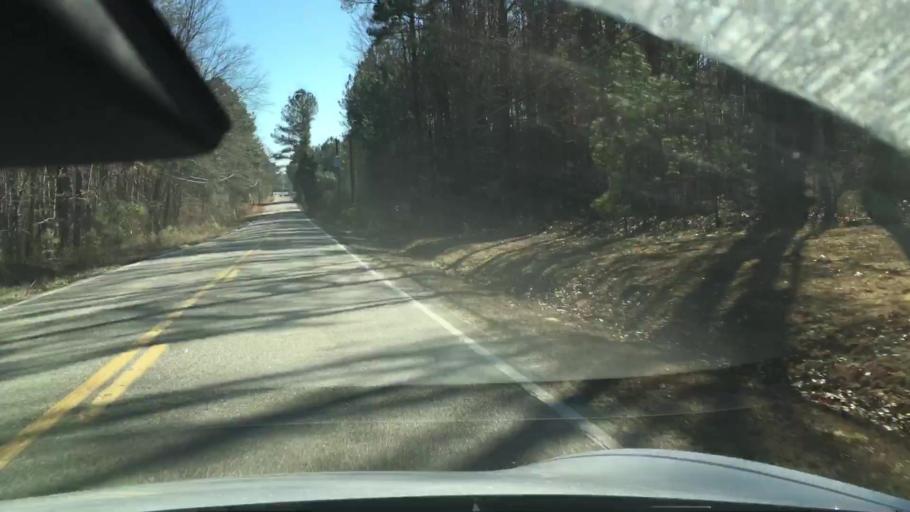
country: US
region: Virginia
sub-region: Henrico County
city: Short Pump
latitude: 37.5723
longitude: -77.7174
